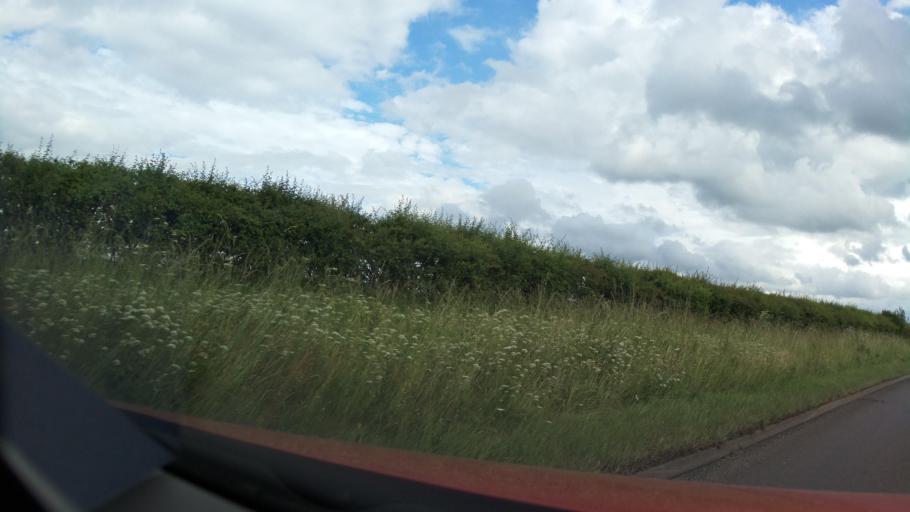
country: GB
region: England
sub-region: Worcestershire
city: Kidderminster
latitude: 52.4403
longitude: -2.2116
